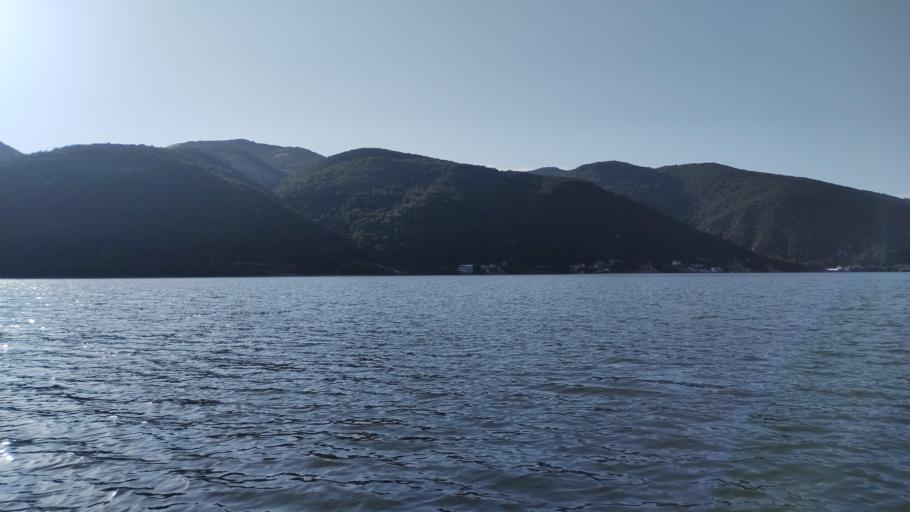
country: RO
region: Mehedinti
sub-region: Comuna Dubova
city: Dubova
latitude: 44.5592
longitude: 22.2326
